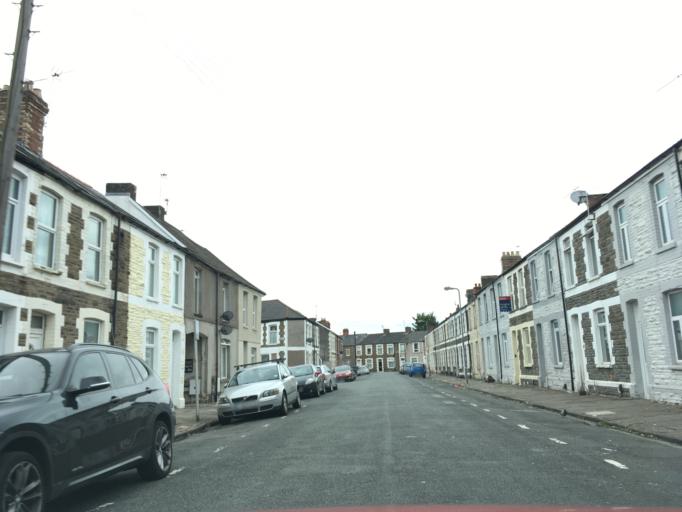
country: GB
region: Wales
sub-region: Cardiff
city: Cardiff
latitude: 51.4932
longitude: -3.1834
